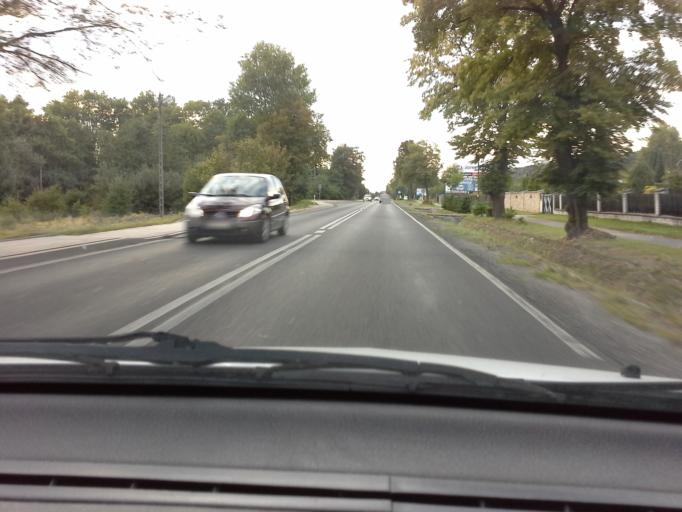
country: PL
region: Lesser Poland Voivodeship
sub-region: Powiat chrzanowski
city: Psary
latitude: 50.1452
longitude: 19.5073
